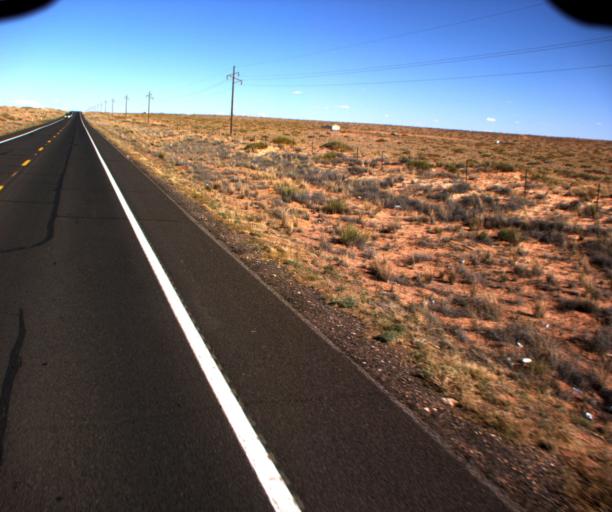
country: US
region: Arizona
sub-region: Coconino County
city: Tuba City
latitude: 36.1369
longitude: -111.1715
